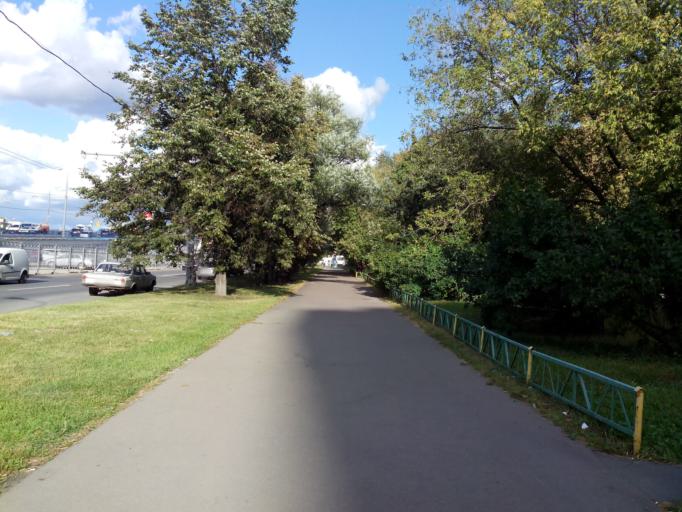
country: RU
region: Moskovskaya
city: Bogorodskoye
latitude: 55.8001
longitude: 37.7422
